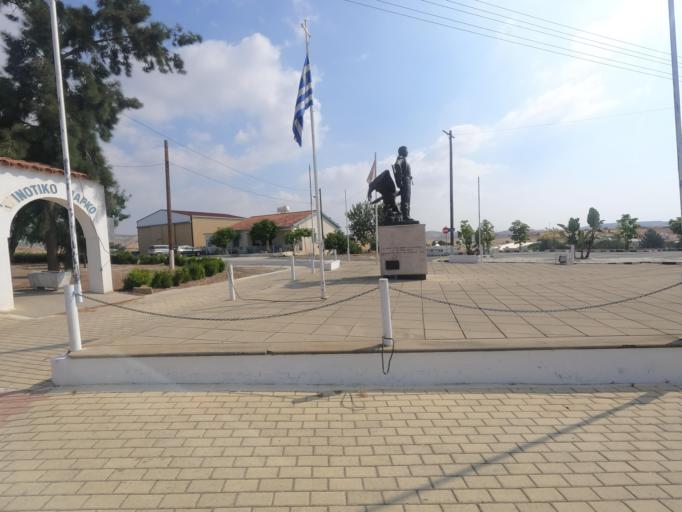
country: CY
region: Larnaka
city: Aradippou
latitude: 34.9301
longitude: 33.5350
